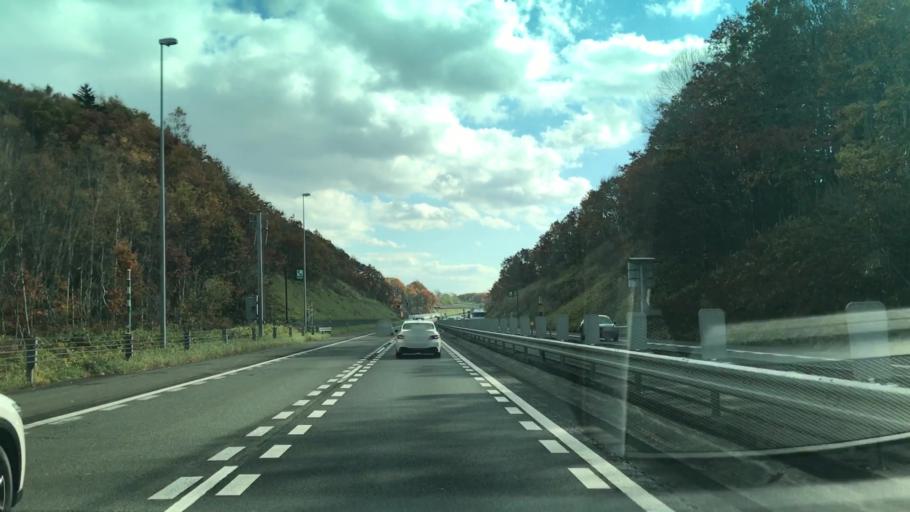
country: JP
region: Hokkaido
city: Kitahiroshima
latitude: 42.9269
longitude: 141.5372
